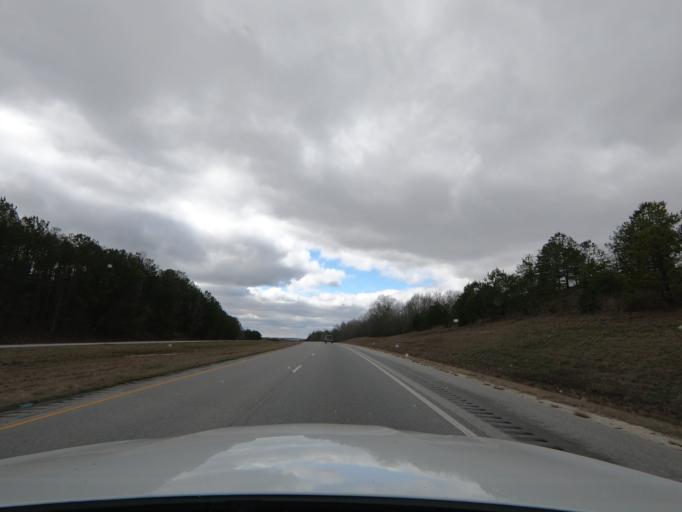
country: US
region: Alabama
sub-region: Russell County
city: Ladonia
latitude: 32.4012
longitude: -85.0614
